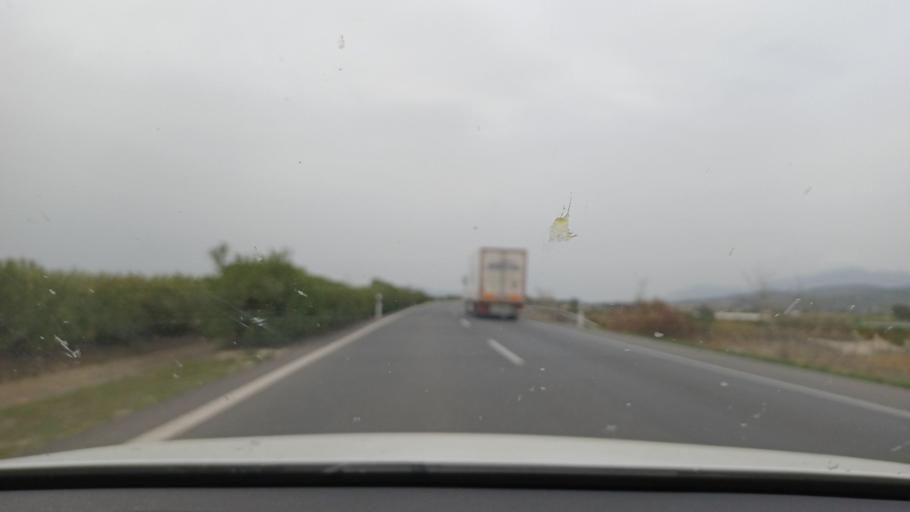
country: ES
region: Catalonia
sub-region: Provincia de Tarragona
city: Ulldecona
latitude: 40.5488
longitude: 0.4210
